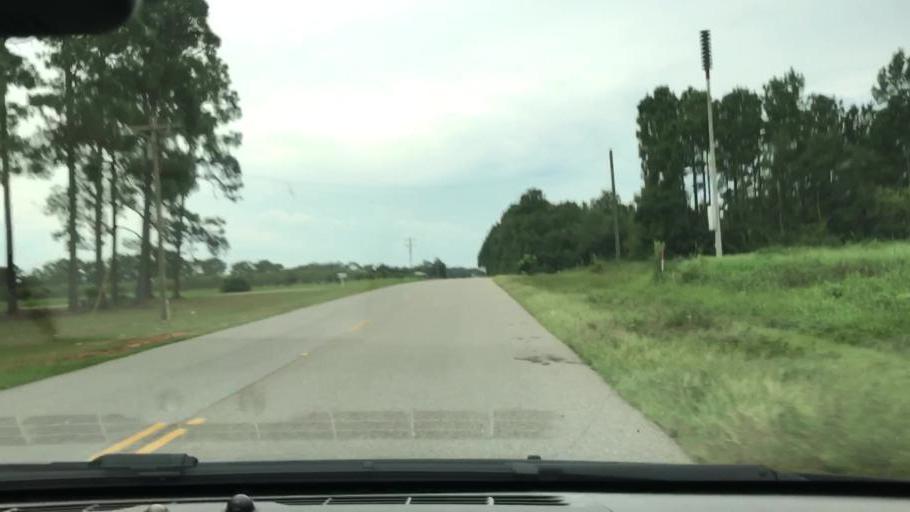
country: US
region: Alabama
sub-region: Houston County
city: Ashford
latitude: 31.2611
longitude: -85.1667
